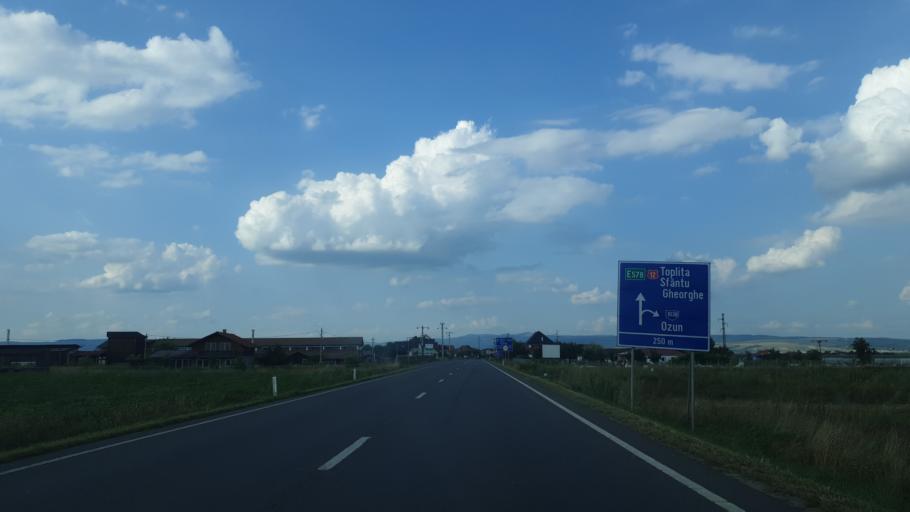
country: RO
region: Covasna
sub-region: Municipiul Sfantu Gheorghe
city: Sfantu-Gheorghe
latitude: 45.8296
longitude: 25.8030
